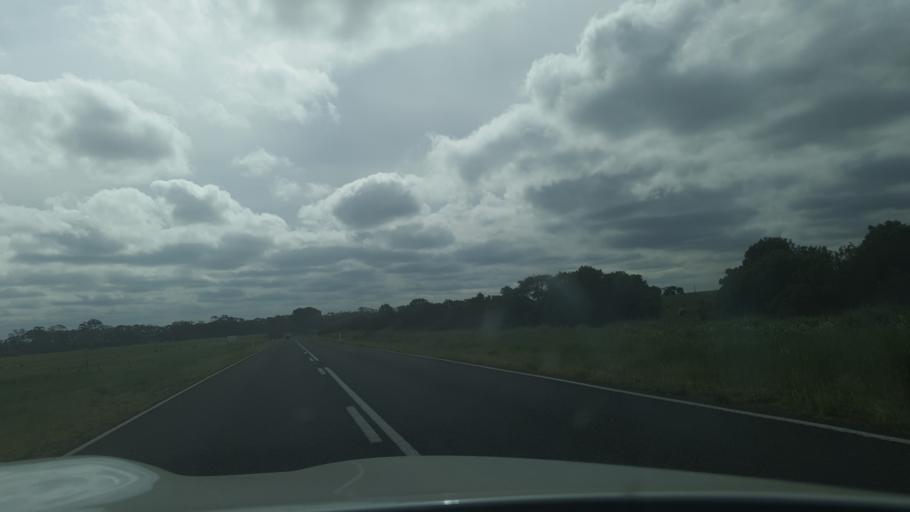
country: AU
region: Victoria
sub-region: Central Goldfields
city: Maryborough
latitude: -37.2075
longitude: 143.7172
